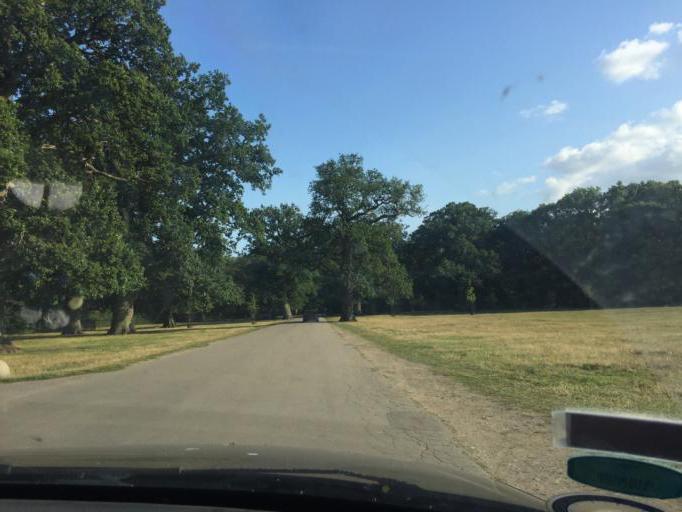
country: DK
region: Zealand
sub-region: Lolland Kommune
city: Maribo
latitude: 54.8150
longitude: 11.5105
